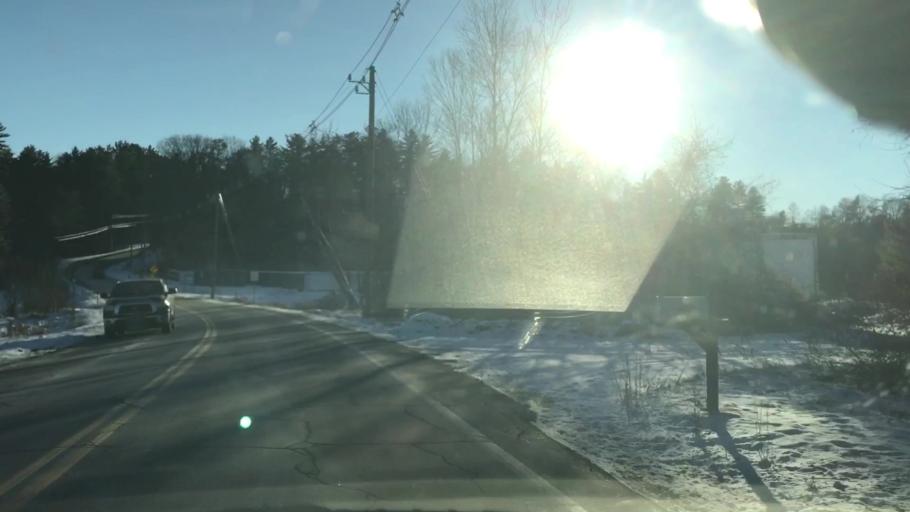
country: US
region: New Hampshire
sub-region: Grafton County
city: North Haverhill
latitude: 44.0751
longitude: -72.0314
